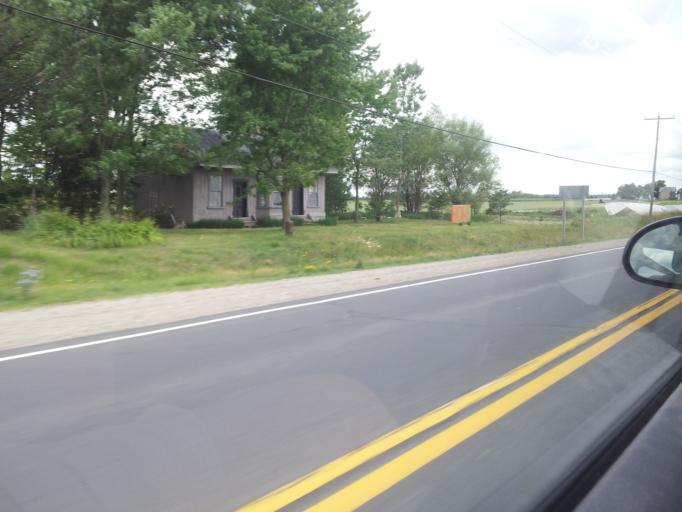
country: CA
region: Ontario
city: Stratford
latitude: 43.3698
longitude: -80.8625
